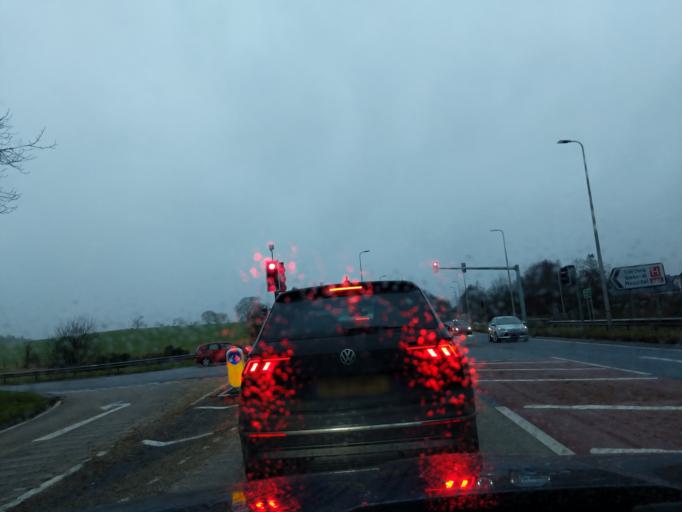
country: GB
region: Scotland
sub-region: The Scottish Borders
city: Melrose
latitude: 55.5982
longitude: -2.7444
